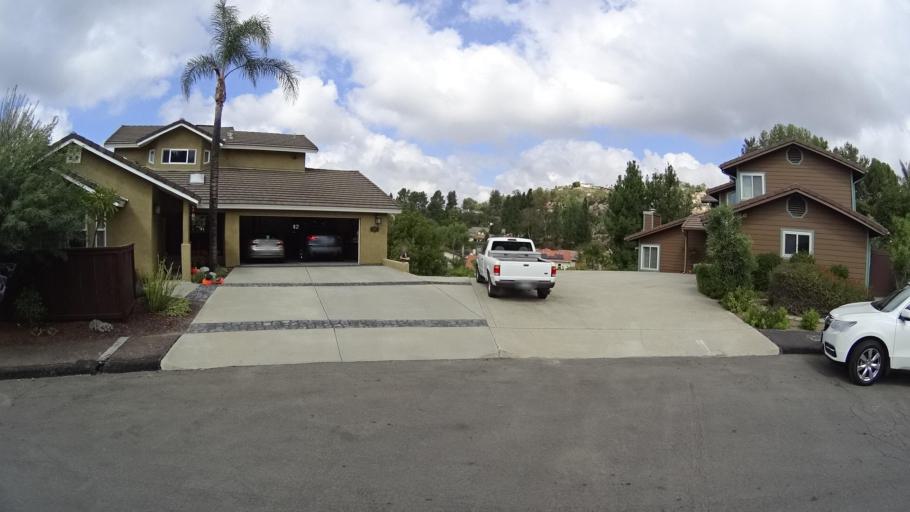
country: US
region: California
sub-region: San Diego County
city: Granite Hills
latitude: 32.7721
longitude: -116.9101
